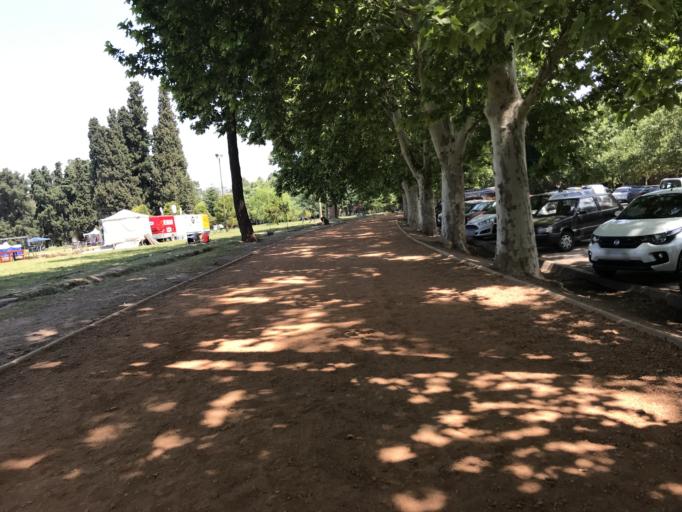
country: AR
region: Mendoza
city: Mendoza
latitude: -32.8965
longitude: -68.8674
